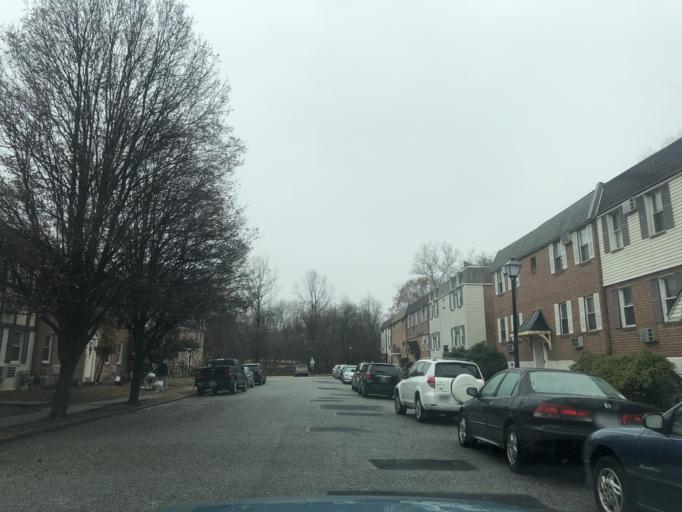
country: US
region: Pennsylvania
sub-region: Delaware County
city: Broomall
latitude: 39.9739
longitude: -75.3394
